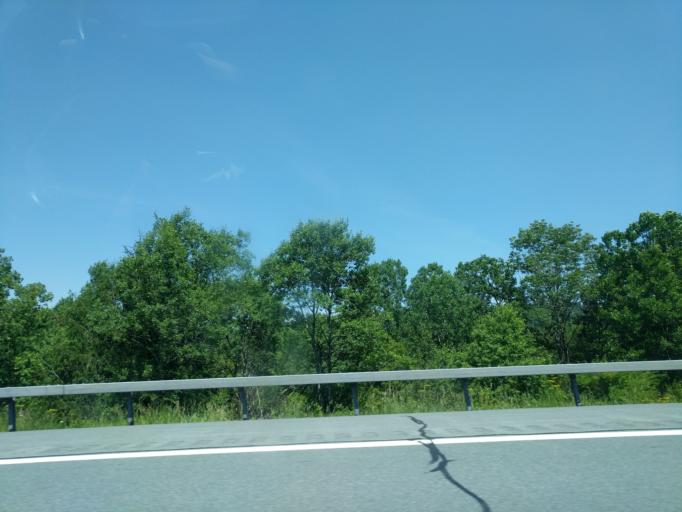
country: US
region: New York
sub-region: Sullivan County
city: Livingston Manor
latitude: 41.9237
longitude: -74.8407
